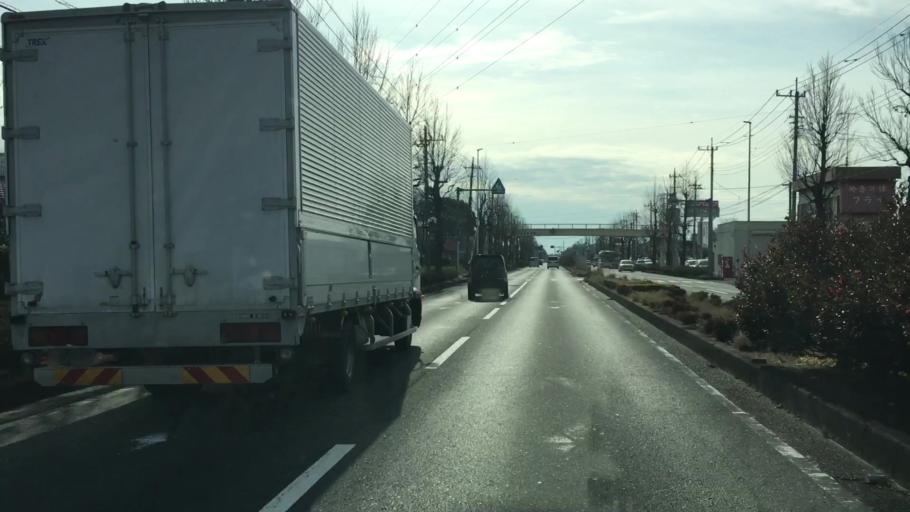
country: JP
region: Saitama
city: Menuma
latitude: 36.1900
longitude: 139.3703
